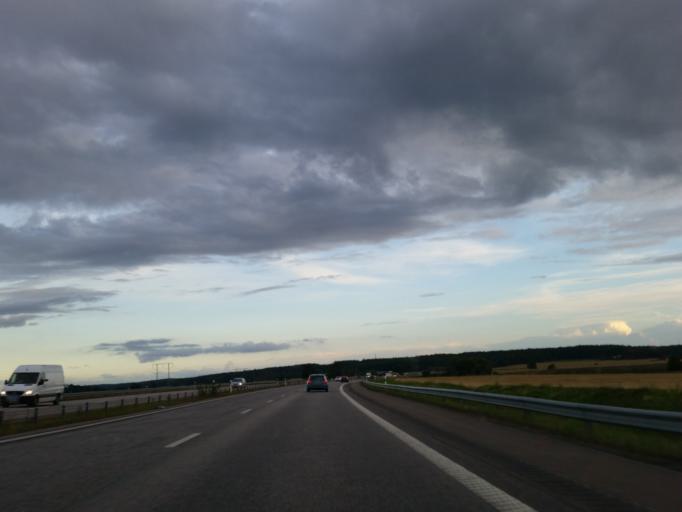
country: SE
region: Uppsala
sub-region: Uppsala Kommun
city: Saevja
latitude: 59.8200
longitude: 17.7517
